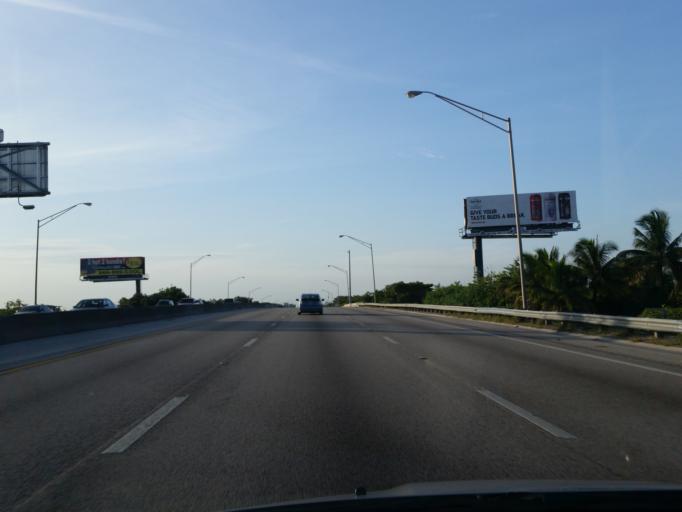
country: US
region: Florida
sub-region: Broward County
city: Pembroke Pines
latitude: 26.0161
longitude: -80.2127
